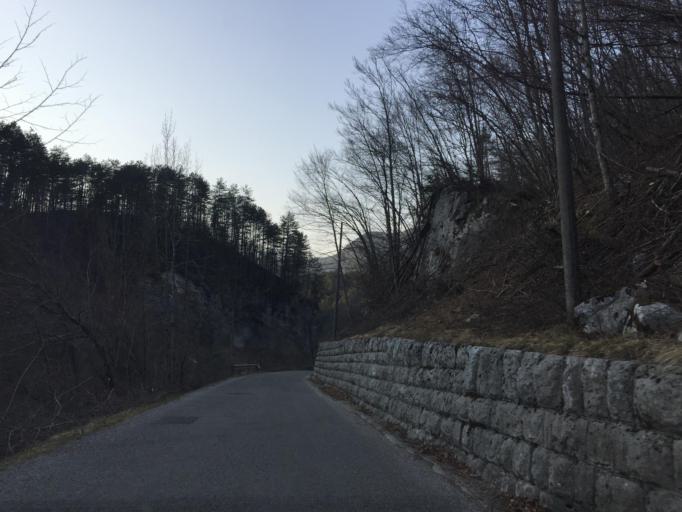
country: IT
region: Friuli Venezia Giulia
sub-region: Provincia di Udine
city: Prato
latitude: 46.3680
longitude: 13.2956
